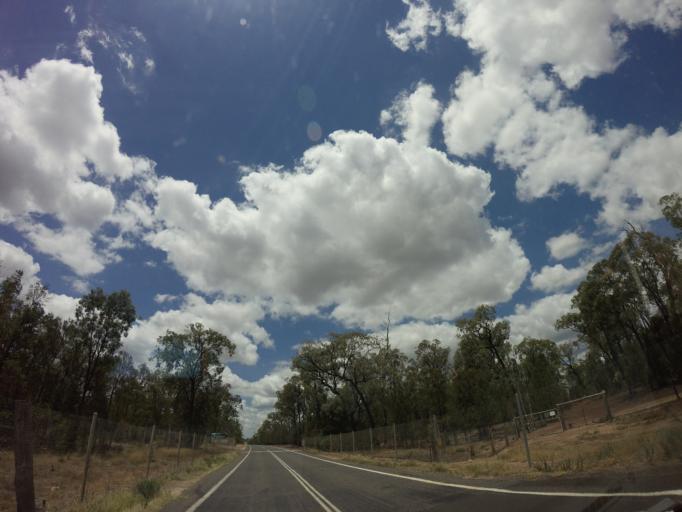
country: AU
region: Queensland
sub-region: Goondiwindi
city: Goondiwindi
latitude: -28.0303
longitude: 150.8318
